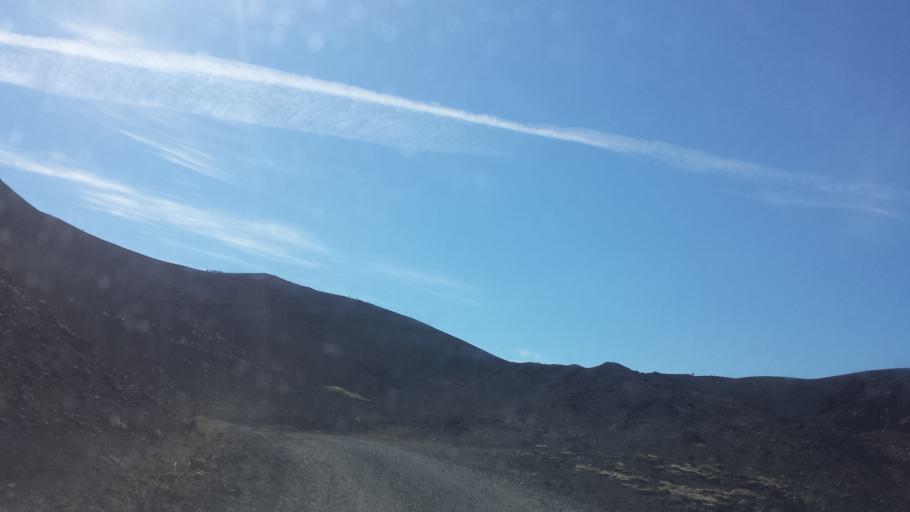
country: IS
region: South
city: Vestmannaeyjar
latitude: 63.4364
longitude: -20.2467
